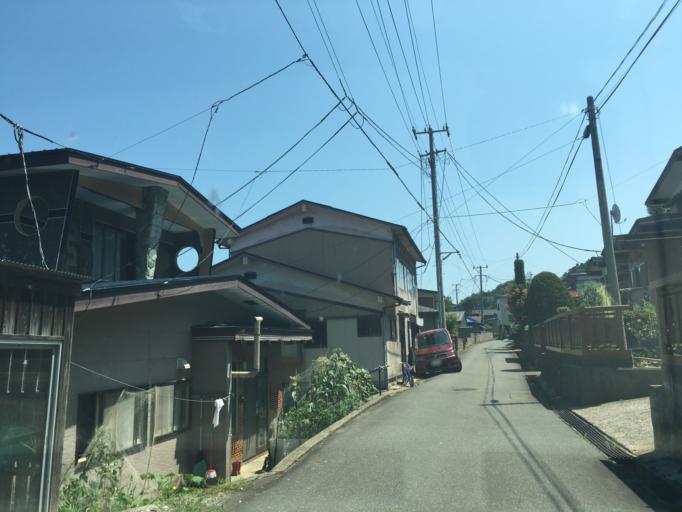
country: JP
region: Akita
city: Tenno
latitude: 39.9991
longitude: 139.7071
